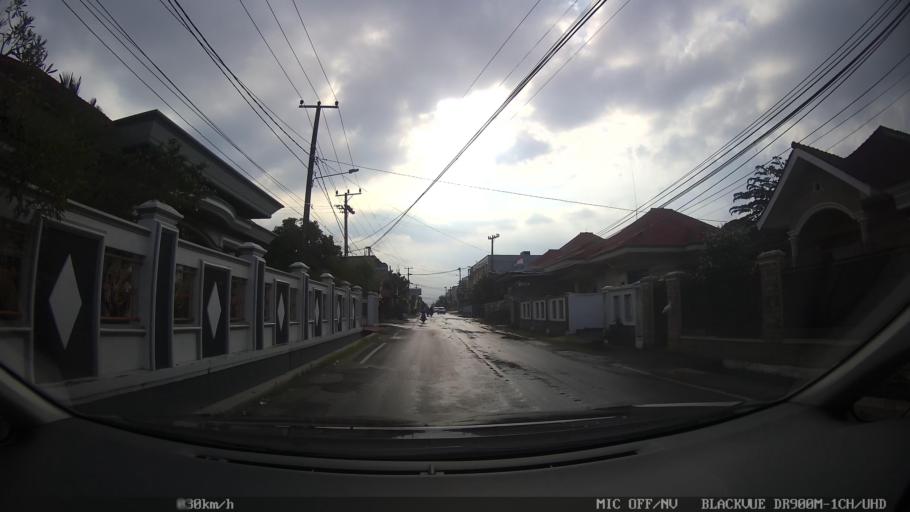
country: ID
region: Lampung
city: Kedaton
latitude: -5.3910
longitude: 105.3039
